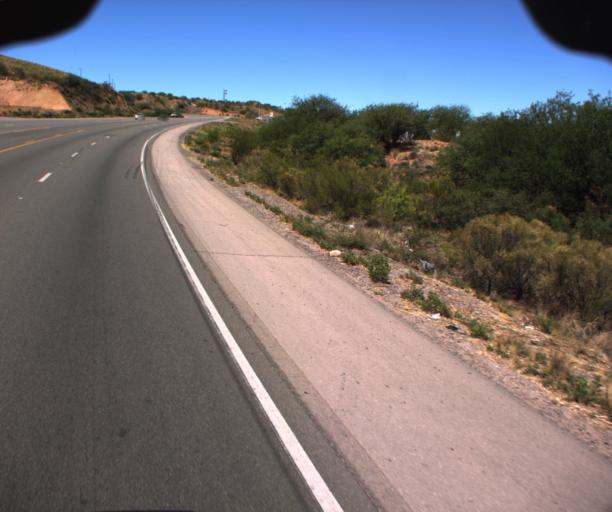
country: US
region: Arizona
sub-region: Santa Cruz County
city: Nogales
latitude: 31.3520
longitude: -110.9607
